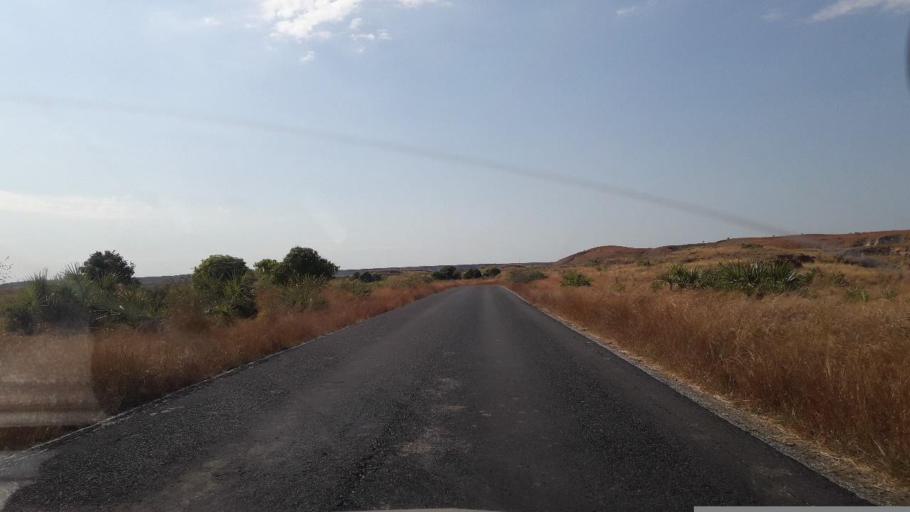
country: MG
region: Boeny
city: Marovoay
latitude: -15.9254
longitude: 46.6444
